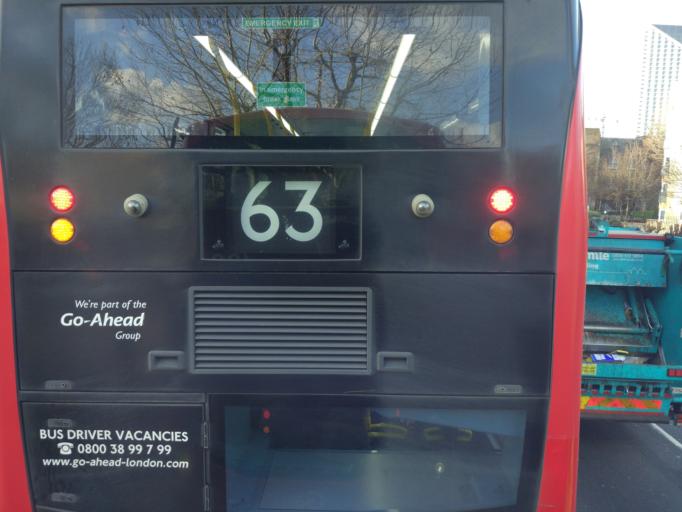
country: GB
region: England
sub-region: Greater London
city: Kennington
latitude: 51.4942
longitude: -0.0945
